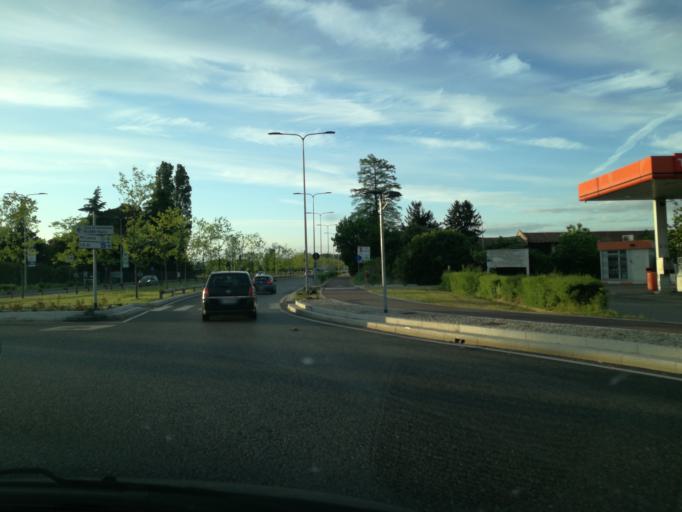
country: IT
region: Lombardy
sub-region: Citta metropolitana di Milano
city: Noverasco-Sporting Mirasole
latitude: 45.4003
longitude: 9.2097
